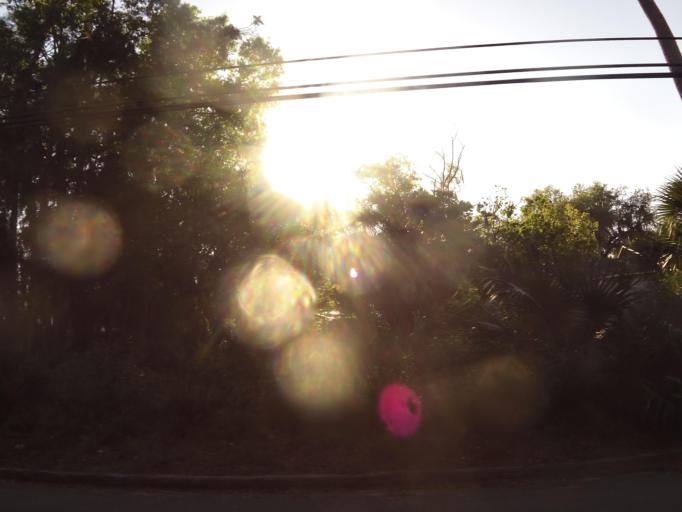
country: US
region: Florida
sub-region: Putnam County
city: Palatka
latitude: 29.6478
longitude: -81.6499
